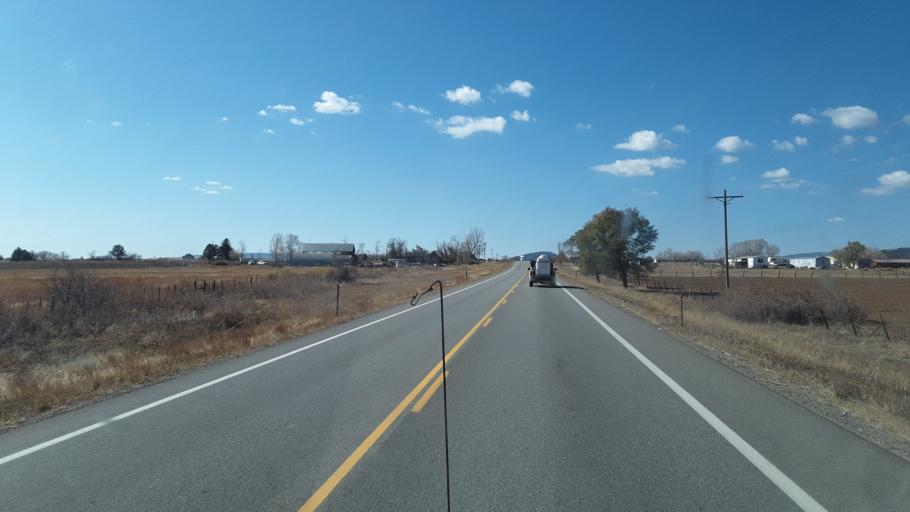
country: US
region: Colorado
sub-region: La Plata County
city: Durango
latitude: 37.2299
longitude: -107.7694
